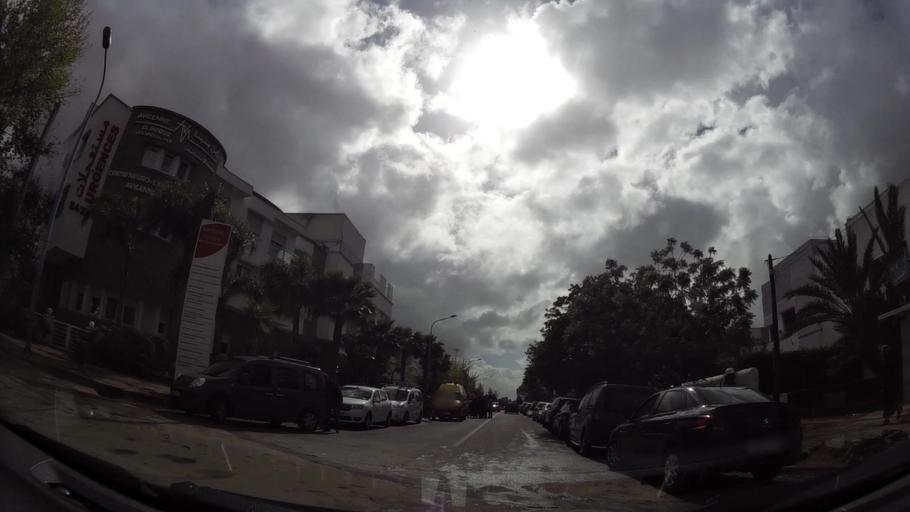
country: MA
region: Grand Casablanca
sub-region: Casablanca
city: Casablanca
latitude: 33.5546
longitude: -7.6108
